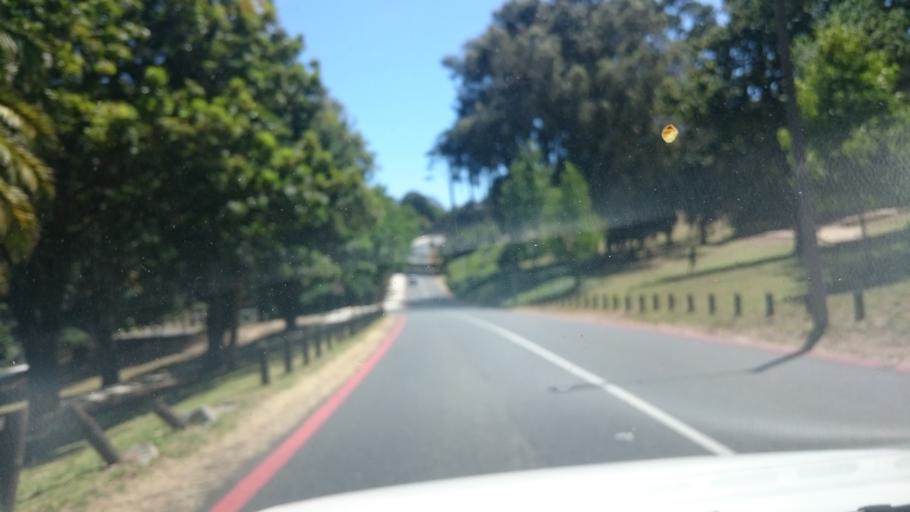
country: ZA
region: Western Cape
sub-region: City of Cape Town
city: Newlands
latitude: -33.9995
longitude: 18.4517
